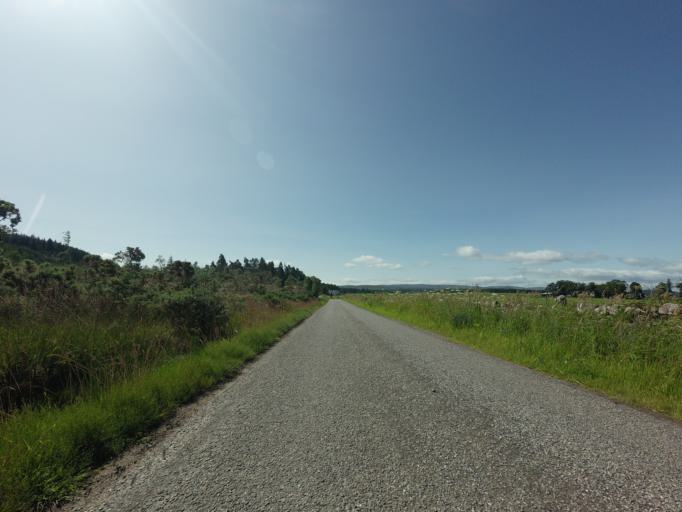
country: GB
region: Scotland
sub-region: Highland
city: Nairn
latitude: 57.5296
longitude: -3.8620
